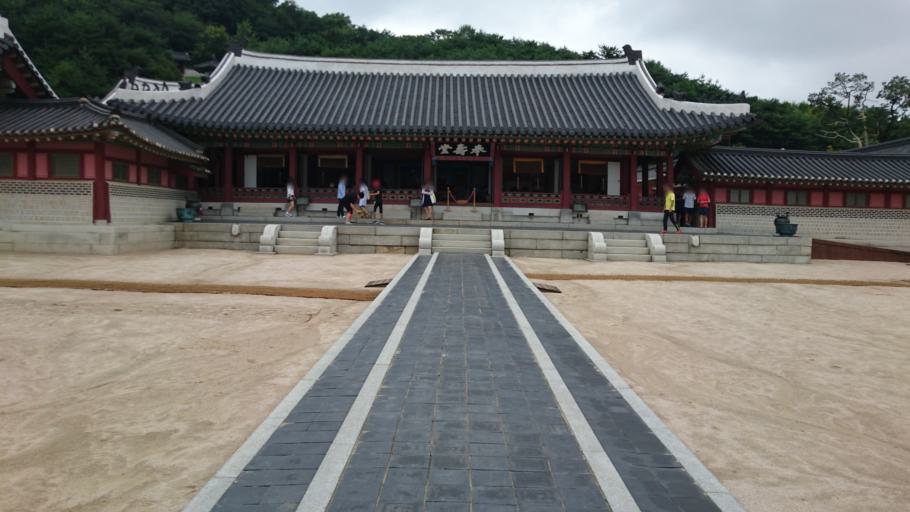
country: KR
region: Gyeonggi-do
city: Suwon-si
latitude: 37.2819
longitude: 127.0135
